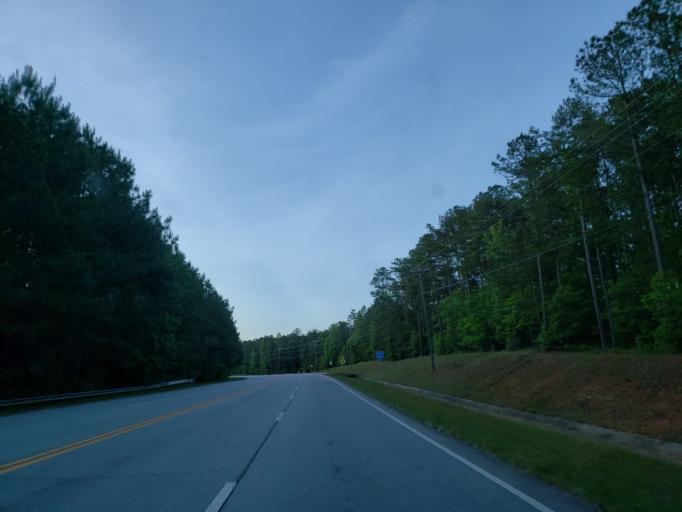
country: US
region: Georgia
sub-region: Fulton County
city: Chattahoochee Hills
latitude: 33.6370
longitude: -84.8305
